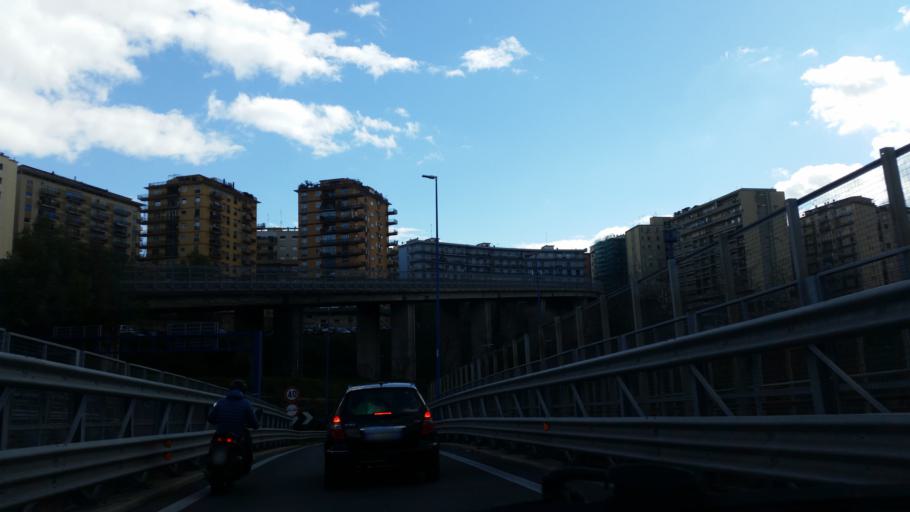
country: IT
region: Campania
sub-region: Provincia di Napoli
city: Napoli
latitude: 40.8446
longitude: 14.2180
